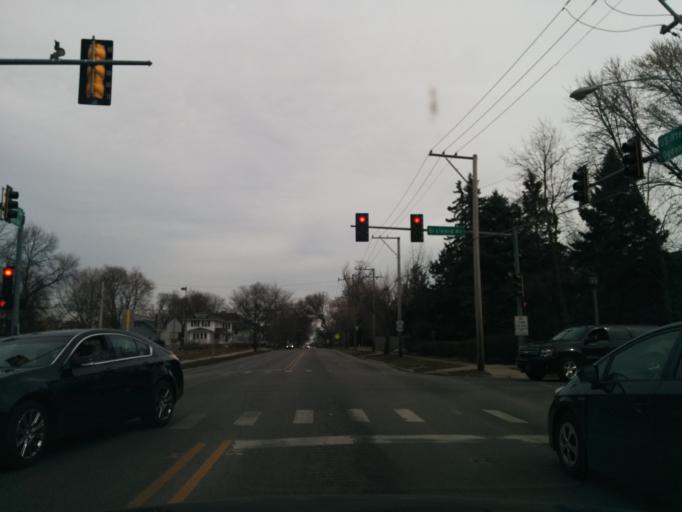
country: US
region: Illinois
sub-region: Cook County
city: La Grange
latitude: 41.8188
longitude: -87.8801
